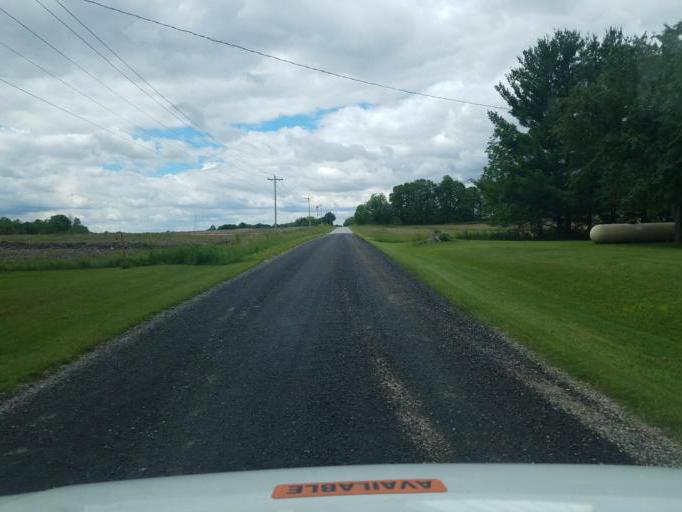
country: US
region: Ohio
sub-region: Crawford County
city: Galion
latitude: 40.6529
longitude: -82.7109
